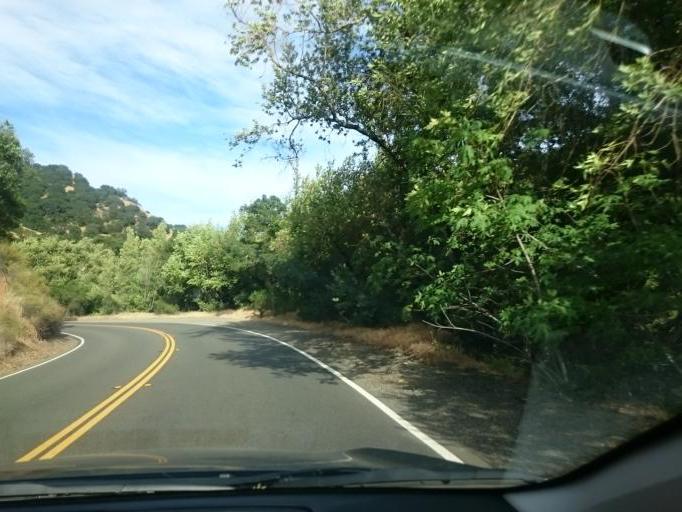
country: US
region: California
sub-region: Napa County
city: Yountville
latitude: 38.4898
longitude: -122.3240
